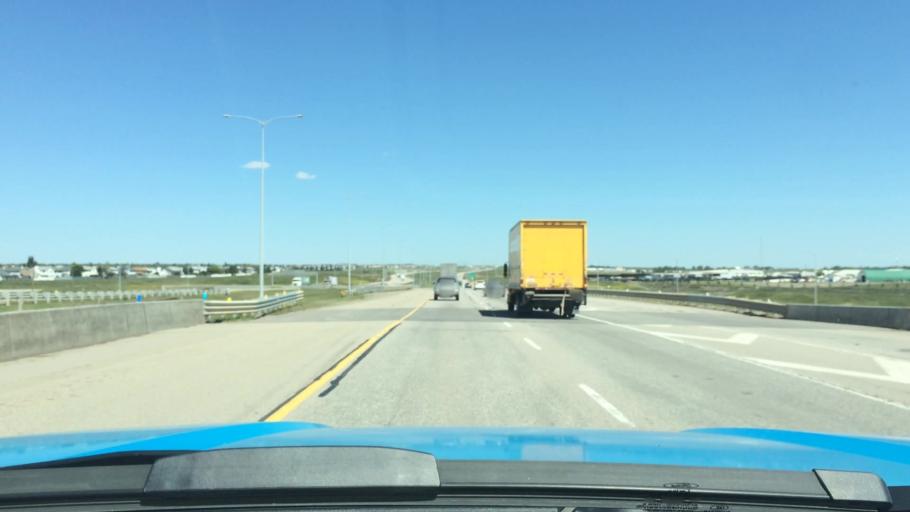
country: CA
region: Alberta
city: Chestermere
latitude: 51.0671
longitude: -113.9202
